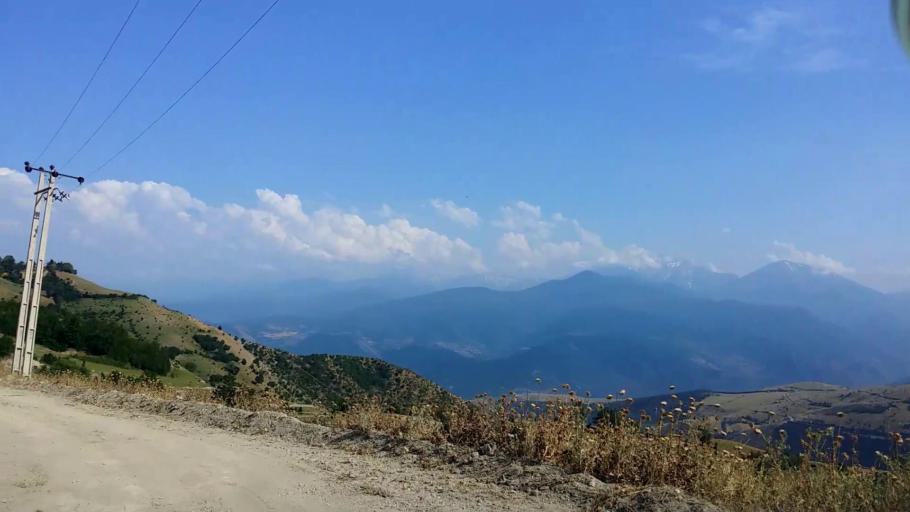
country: IR
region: Mazandaran
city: Chalus
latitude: 36.5490
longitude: 51.2947
